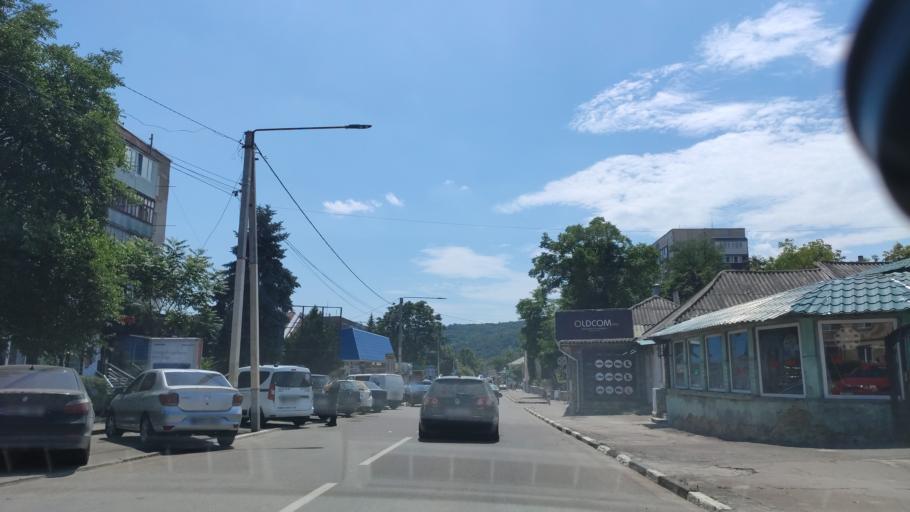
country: MD
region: Raionul Soroca
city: Soroca
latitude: 48.1616
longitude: 28.3013
